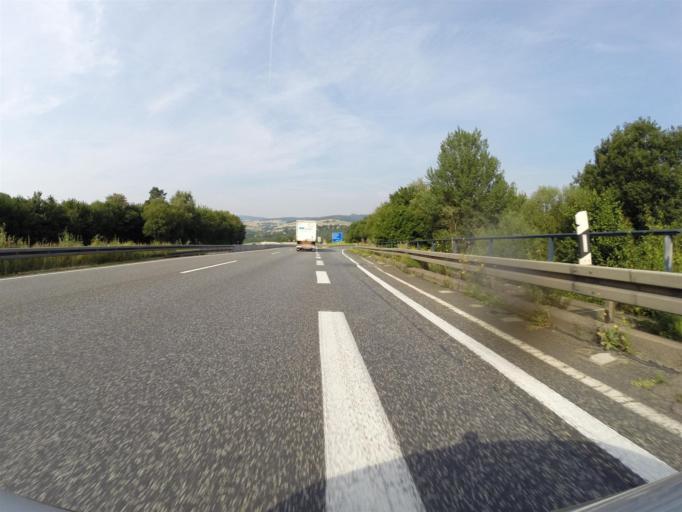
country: DE
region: Hesse
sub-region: Regierungsbezirk Kassel
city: Kirchheim
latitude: 50.8488
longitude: 9.5856
